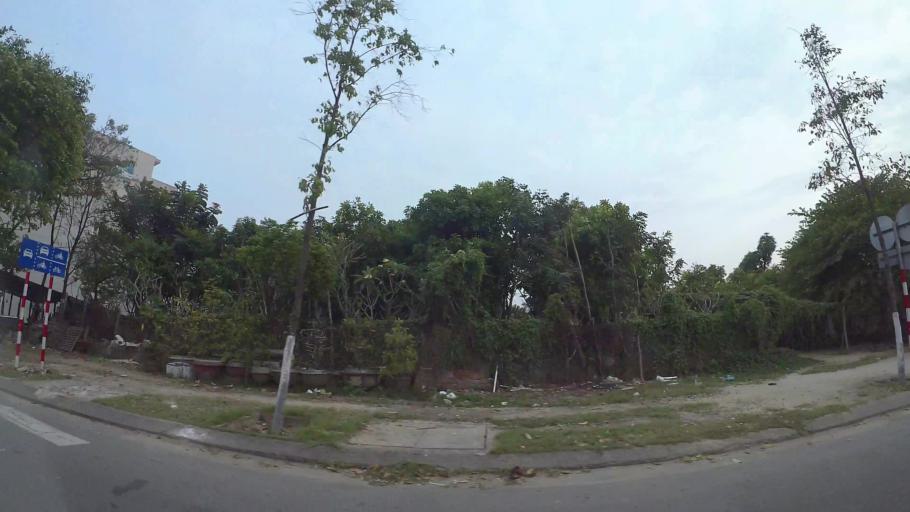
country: VN
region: Da Nang
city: Cam Le
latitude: 16.0312
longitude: 108.2094
